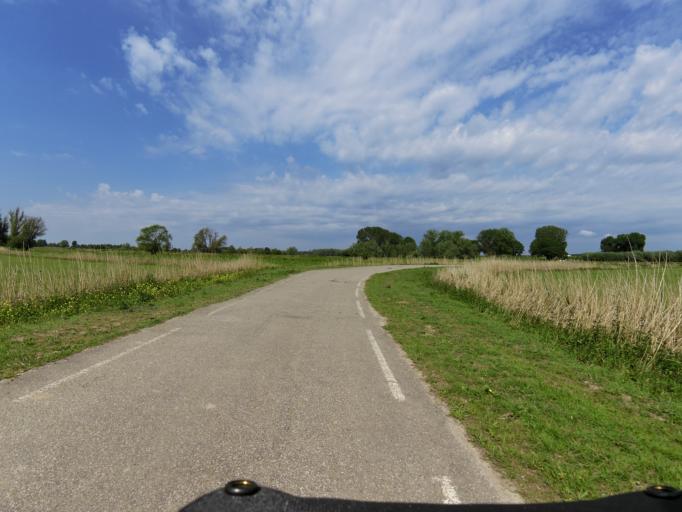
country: NL
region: North Brabant
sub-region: Gemeente Woudrichem
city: Woudrichem
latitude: 51.8128
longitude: 5.0266
